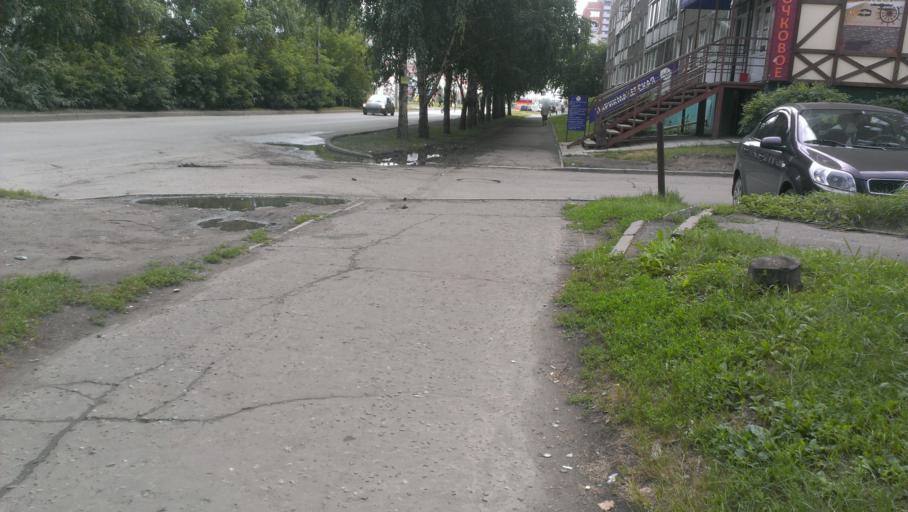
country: RU
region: Altai Krai
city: Novosilikatnyy
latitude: 53.3317
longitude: 83.6760
